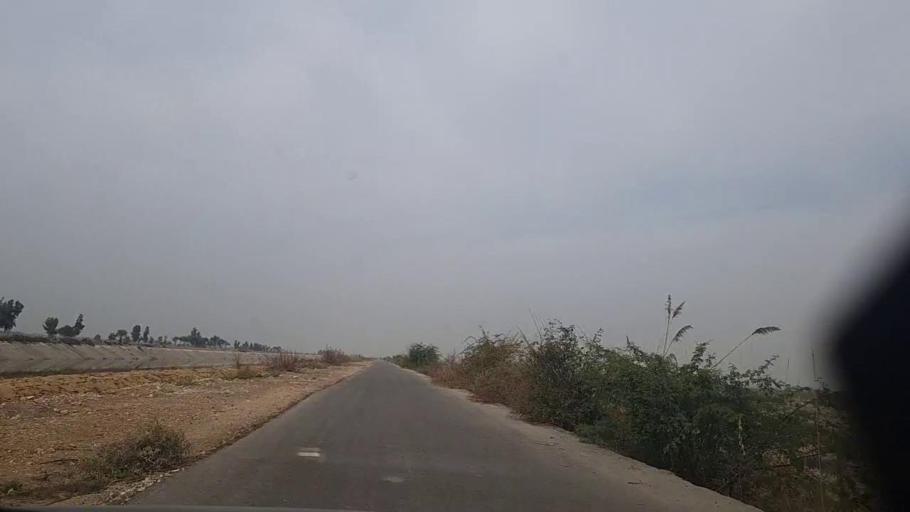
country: PK
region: Sindh
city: Sakrand
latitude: 26.2607
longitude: 68.2429
